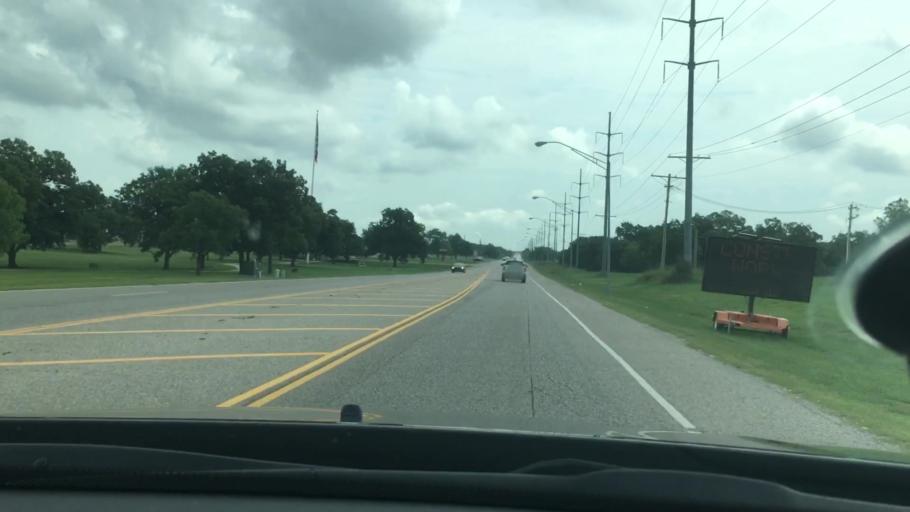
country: US
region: Oklahoma
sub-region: Carter County
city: Ardmore
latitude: 34.2028
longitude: -97.1345
